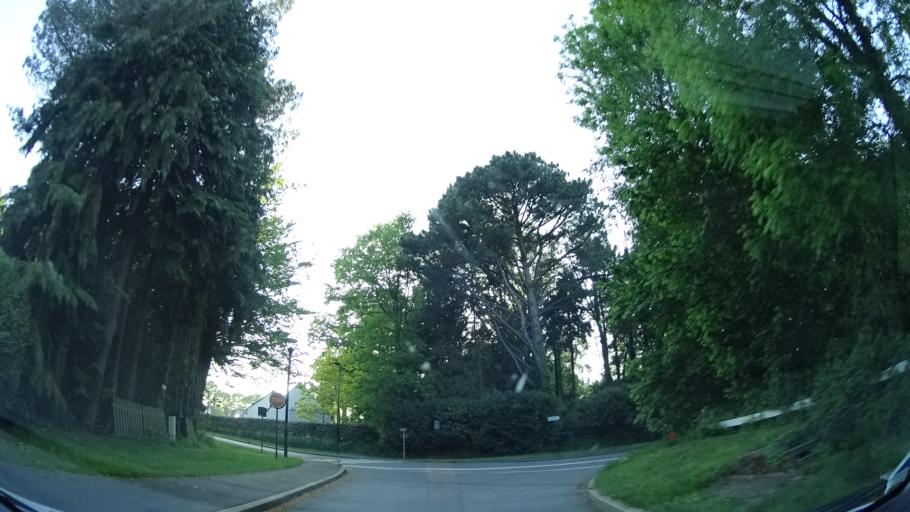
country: FR
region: Brittany
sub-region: Departement d'Ille-et-Vilaine
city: Pace
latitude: 48.1500
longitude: -1.7596
